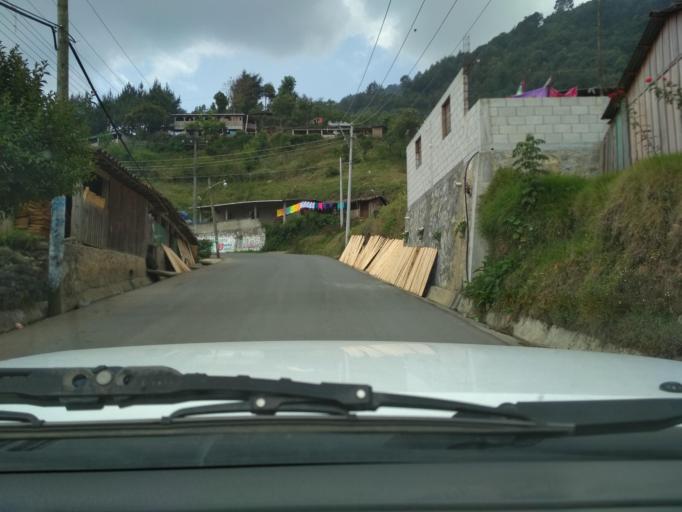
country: MX
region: Veracruz
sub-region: Camerino Z. Mendoza
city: Necoxtla
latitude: 18.7770
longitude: -97.1538
